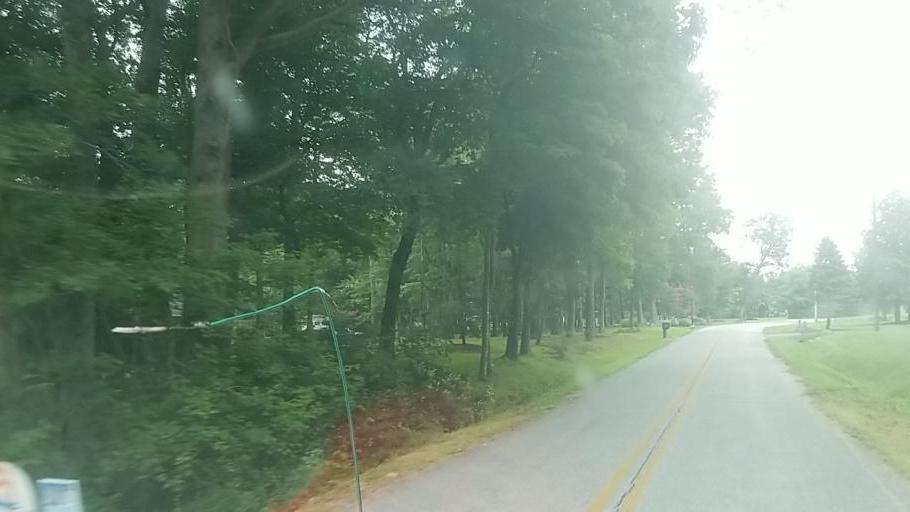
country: US
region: Maryland
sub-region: Worcester County
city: Ocean Pines
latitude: 38.4212
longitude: -75.1903
